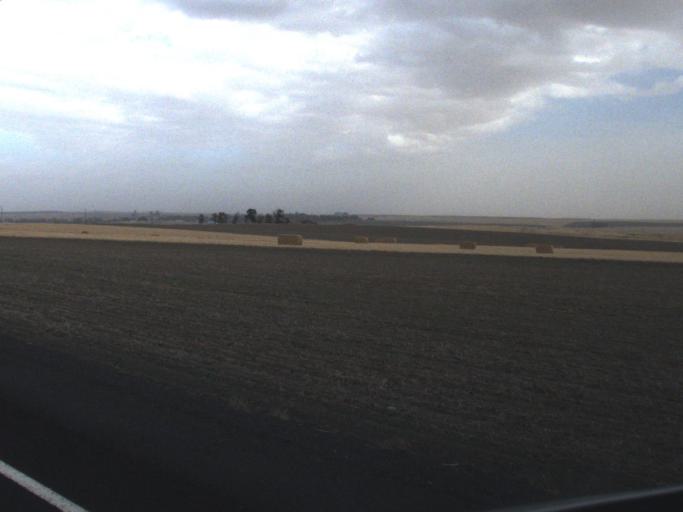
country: US
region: Washington
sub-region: Lincoln County
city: Davenport
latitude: 47.4614
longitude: -118.3042
